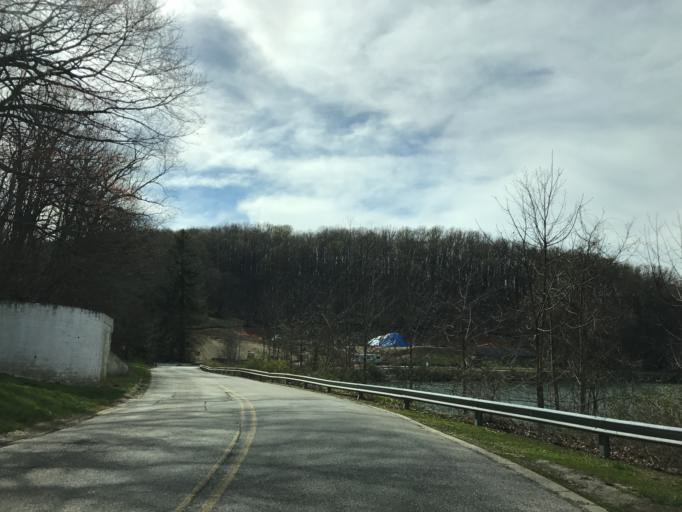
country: US
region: Maryland
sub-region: Baltimore County
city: Carney
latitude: 39.4252
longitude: -76.5422
